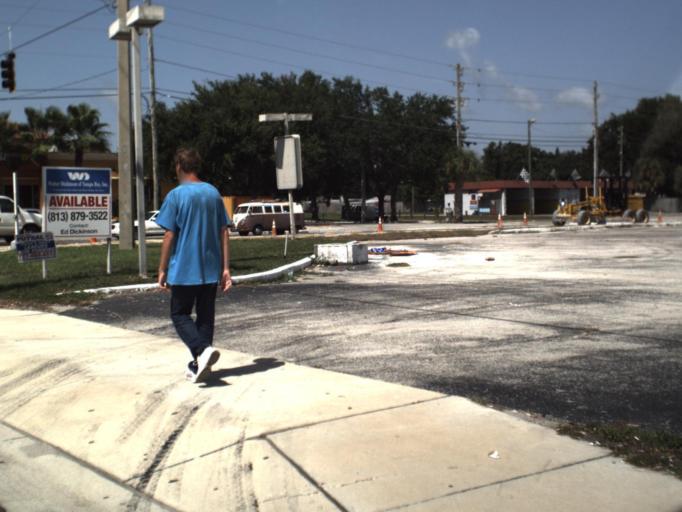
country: US
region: Florida
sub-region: Pinellas County
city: Largo
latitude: 27.9274
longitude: -82.7875
